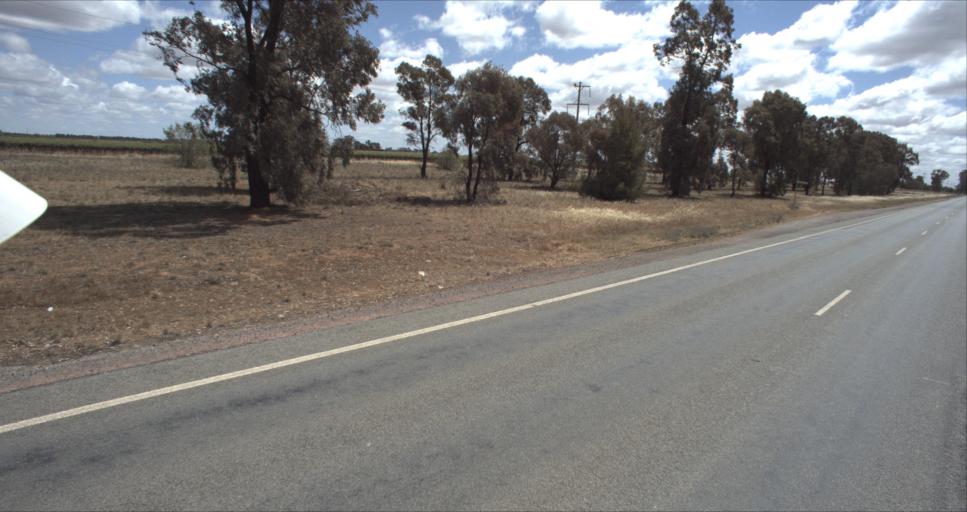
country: AU
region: New South Wales
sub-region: Murrumbidgee Shire
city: Darlington Point
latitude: -34.5083
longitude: 146.1868
